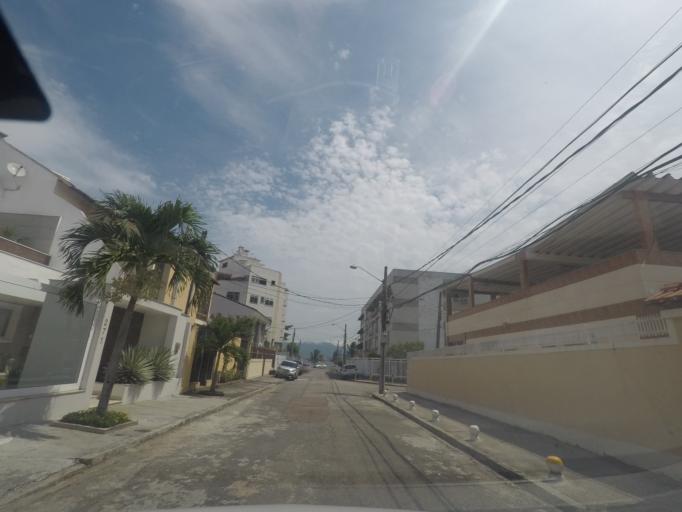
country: BR
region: Rio de Janeiro
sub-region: Rio De Janeiro
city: Rio de Janeiro
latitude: -22.8148
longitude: -43.2117
